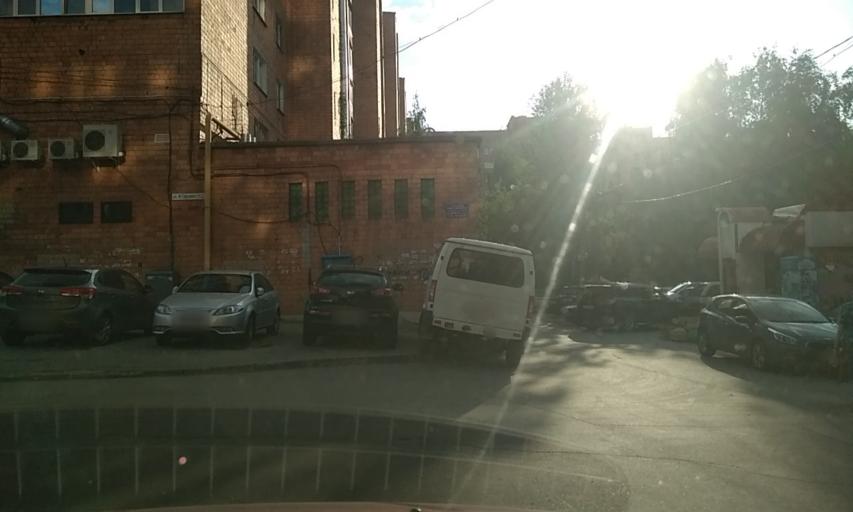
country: RU
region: Nizjnij Novgorod
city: Nizhniy Novgorod
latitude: 56.3166
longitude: 44.0058
